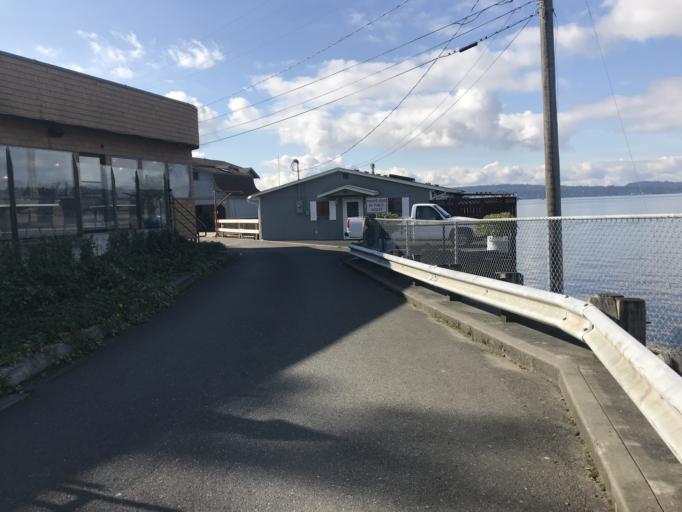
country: US
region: Washington
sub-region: Pierce County
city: University Place
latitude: 47.2465
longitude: -122.5539
